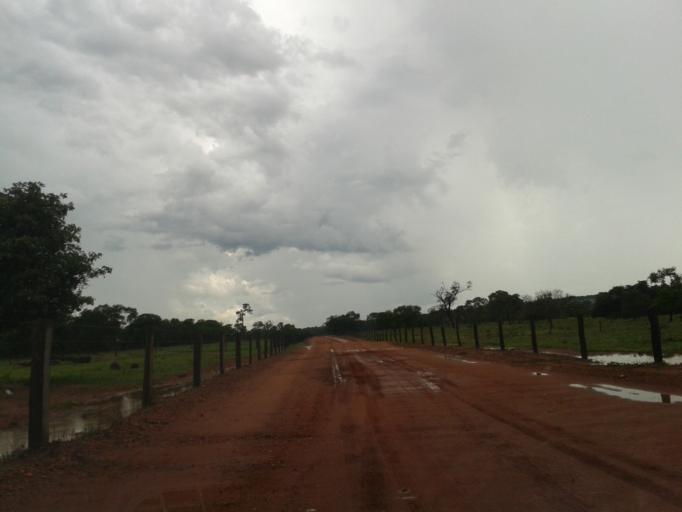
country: BR
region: Minas Gerais
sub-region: Santa Vitoria
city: Santa Vitoria
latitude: -19.1496
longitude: -50.5630
